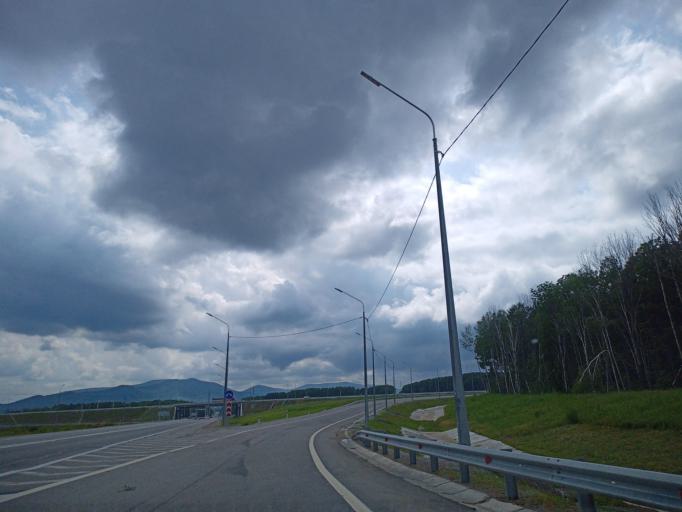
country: RU
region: Khabarovsk Krai
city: Korfovskiy
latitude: 48.2903
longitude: 135.0757
